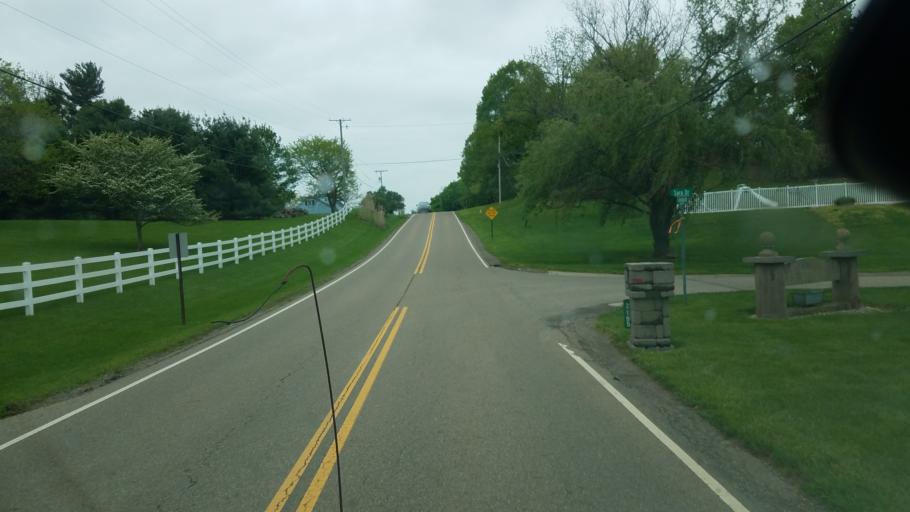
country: US
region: Ohio
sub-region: Coshocton County
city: Coshocton
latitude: 40.2498
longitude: -81.8298
